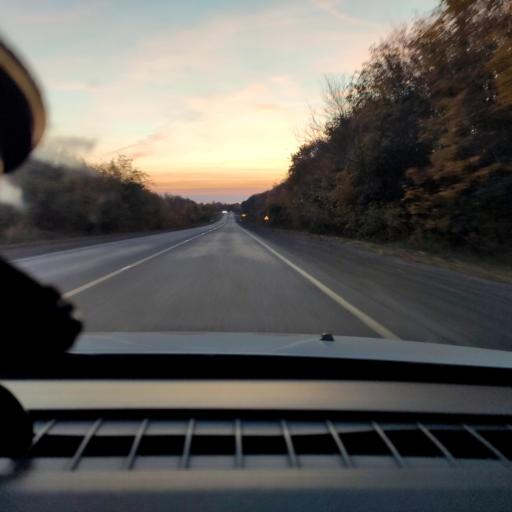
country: RU
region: Samara
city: Novokuybyshevsk
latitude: 52.9826
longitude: 49.8928
